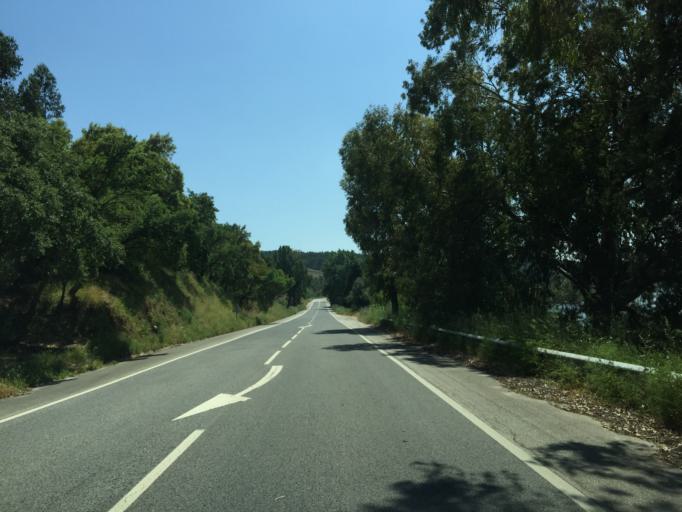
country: PT
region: Santarem
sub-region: Constancia
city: Constancia
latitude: 39.4646
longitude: -8.3418
